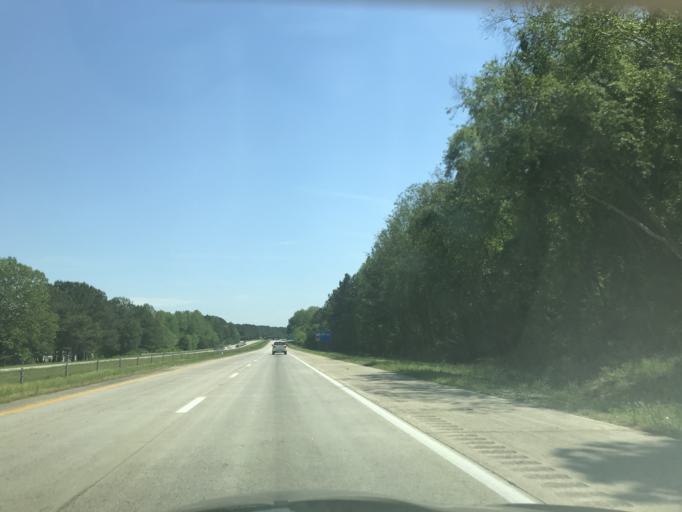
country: US
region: North Carolina
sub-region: Johnston County
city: Benson
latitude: 35.5232
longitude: -78.5626
